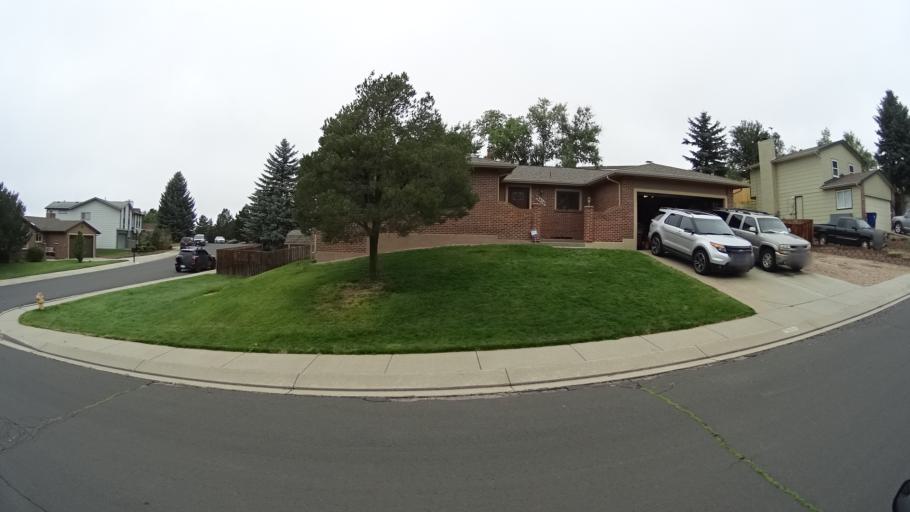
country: US
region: Colorado
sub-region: El Paso County
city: Cimarron Hills
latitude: 38.9340
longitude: -104.7617
